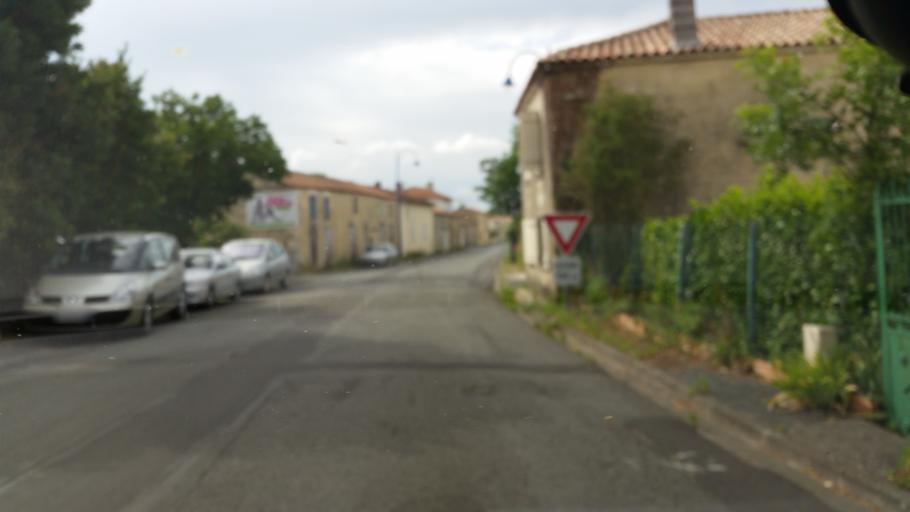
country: FR
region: Poitou-Charentes
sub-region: Departement de la Charente-Maritime
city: Courcon
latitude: 46.1848
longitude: -0.8596
